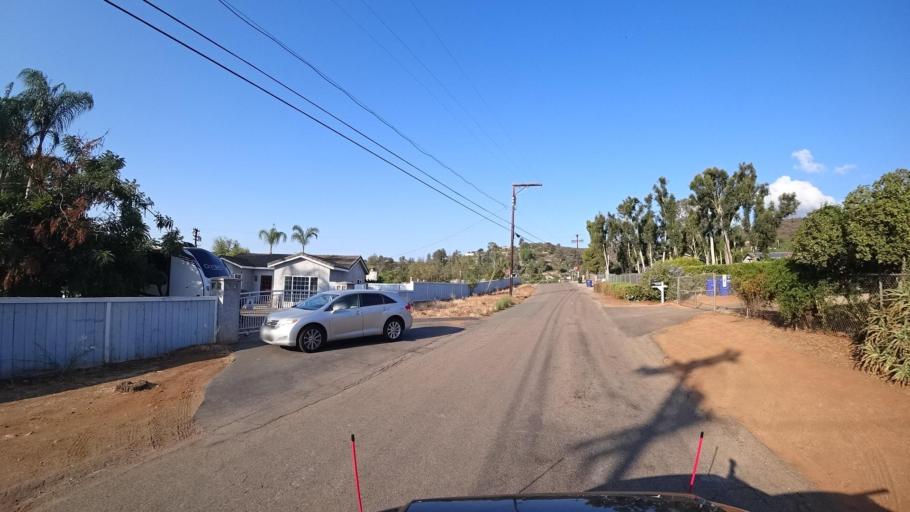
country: US
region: California
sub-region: San Diego County
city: Eucalyptus Hills
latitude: 32.8925
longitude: -116.9457
